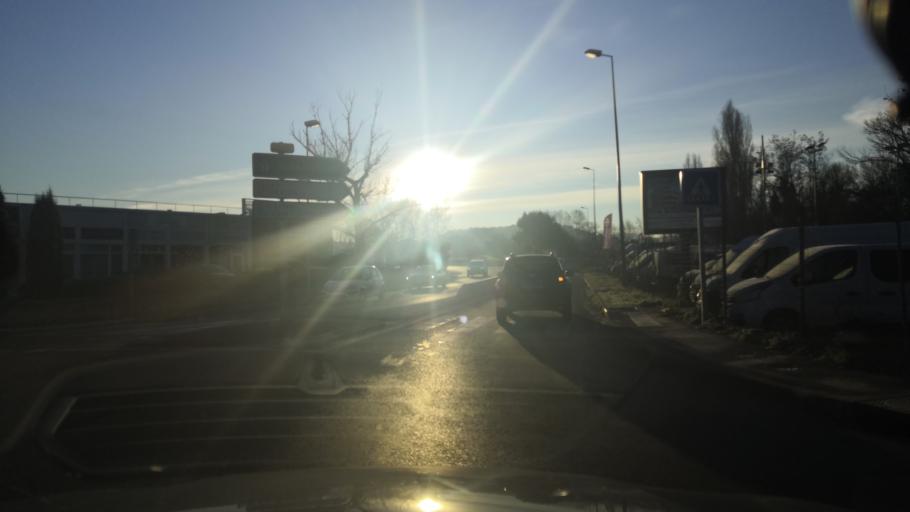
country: FR
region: Provence-Alpes-Cote d'Azur
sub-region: Departement des Bouches-du-Rhone
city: Aix-en-Provence
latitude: 43.5069
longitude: 5.3994
